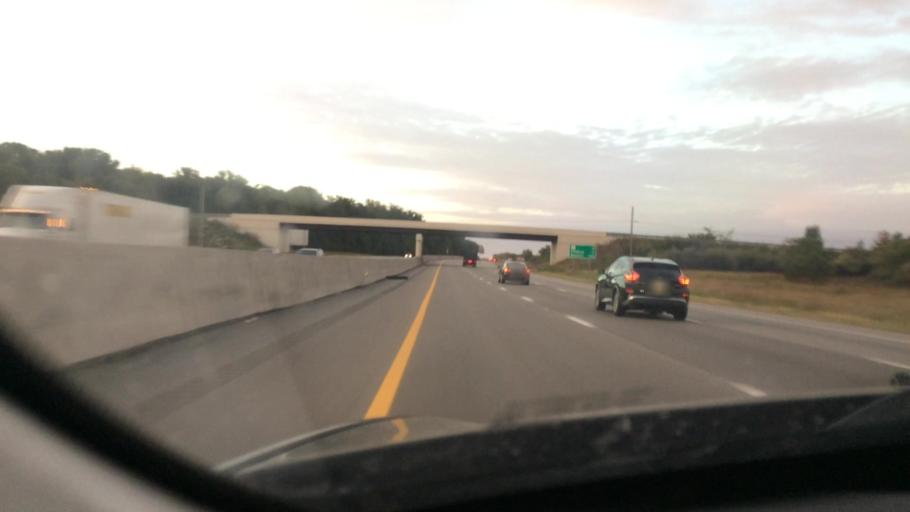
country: US
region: Ohio
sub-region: Wood County
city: North Baltimore
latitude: 41.1256
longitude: -83.6591
